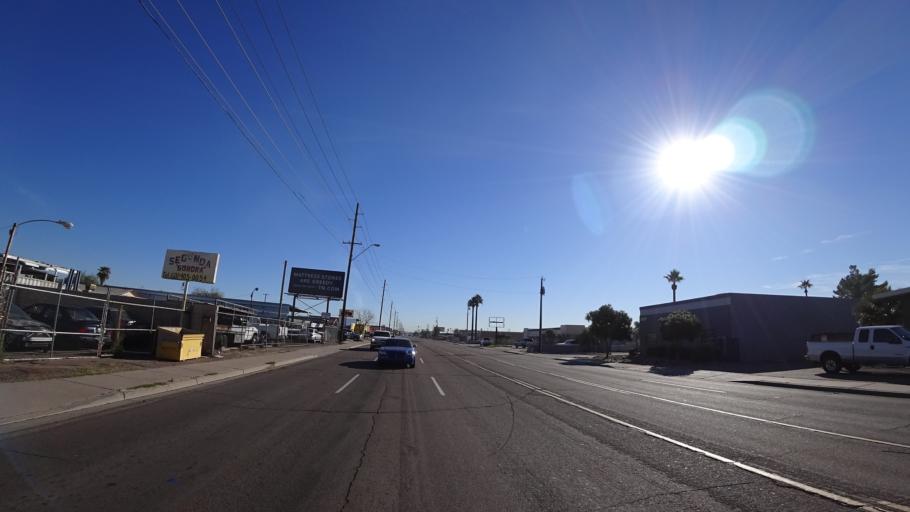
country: US
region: Arizona
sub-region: Maricopa County
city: Phoenix
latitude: 33.4660
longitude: -112.1233
